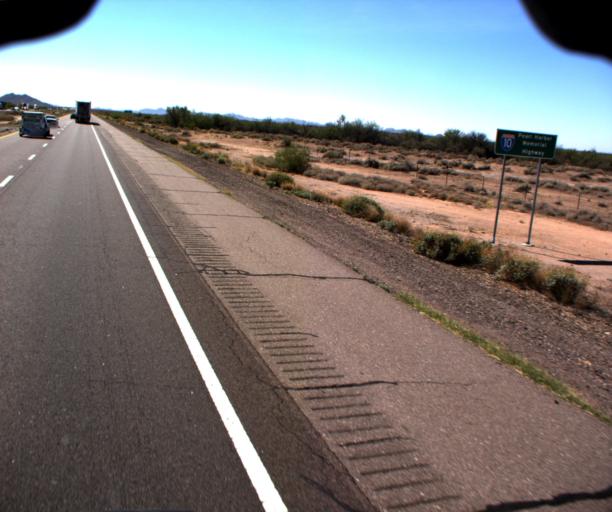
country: US
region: Arizona
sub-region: Maricopa County
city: Sun Lakes
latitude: 33.2063
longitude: -111.9104
